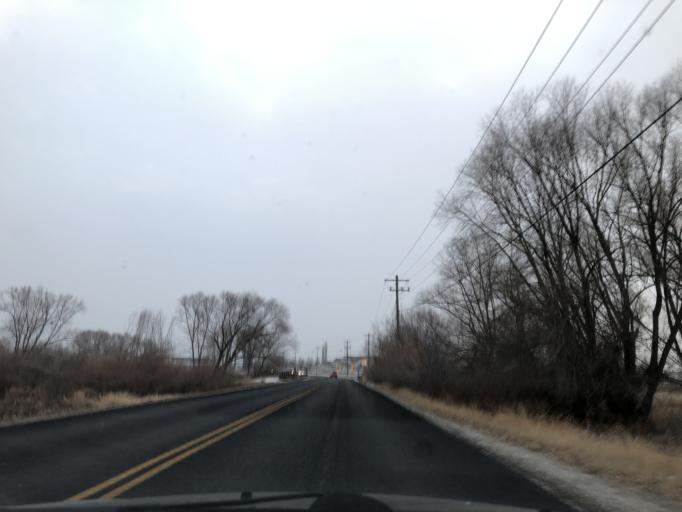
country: US
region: Utah
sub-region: Cache County
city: Logan
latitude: 41.7072
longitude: -111.8531
